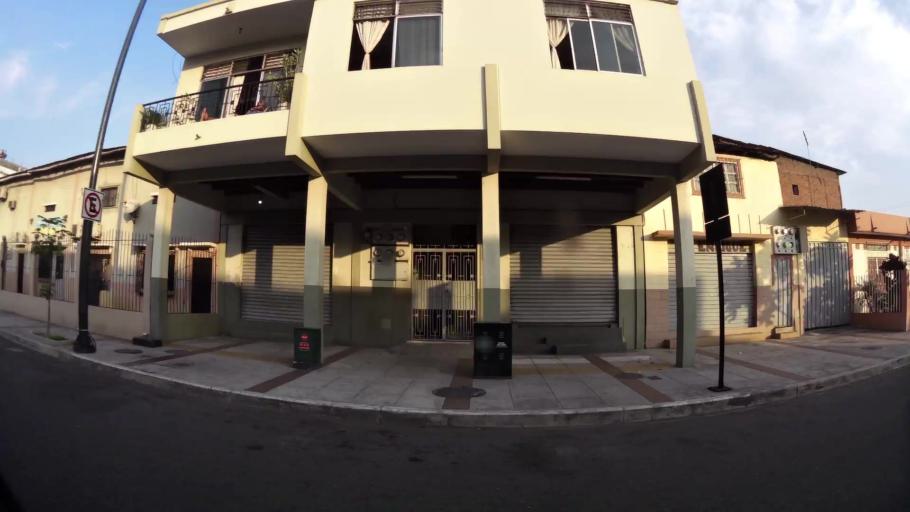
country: EC
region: Guayas
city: Guayaquil
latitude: -2.2048
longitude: -79.8992
